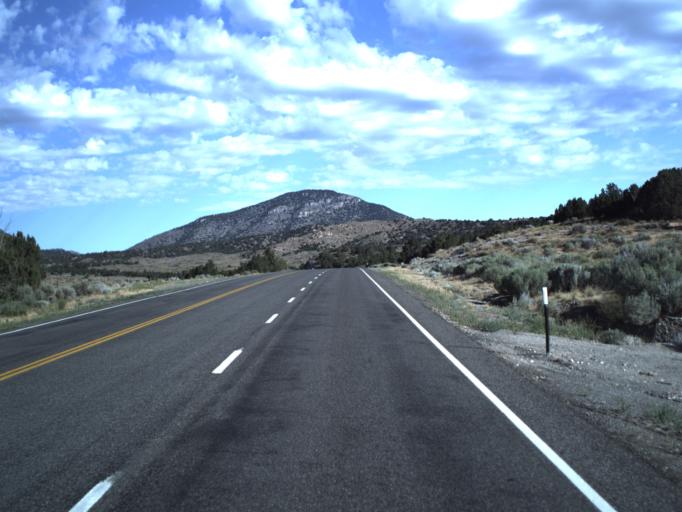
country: US
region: Utah
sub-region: Utah County
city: Genola
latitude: 39.9567
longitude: -112.0351
